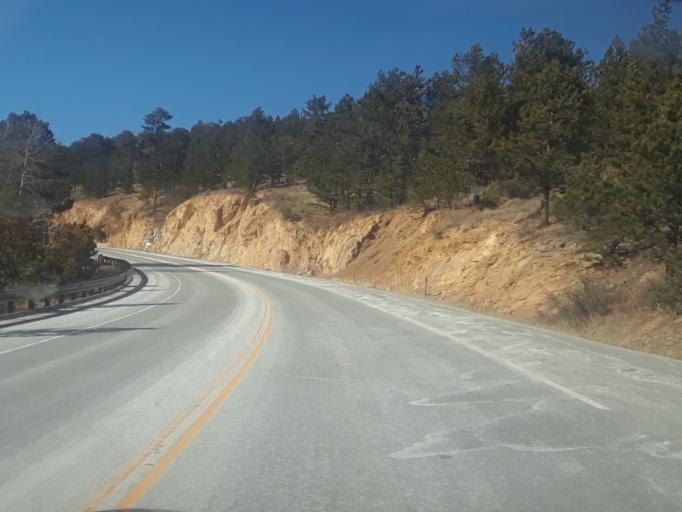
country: US
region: Colorado
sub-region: Larimer County
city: Estes Park
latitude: 40.1921
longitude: -105.5110
